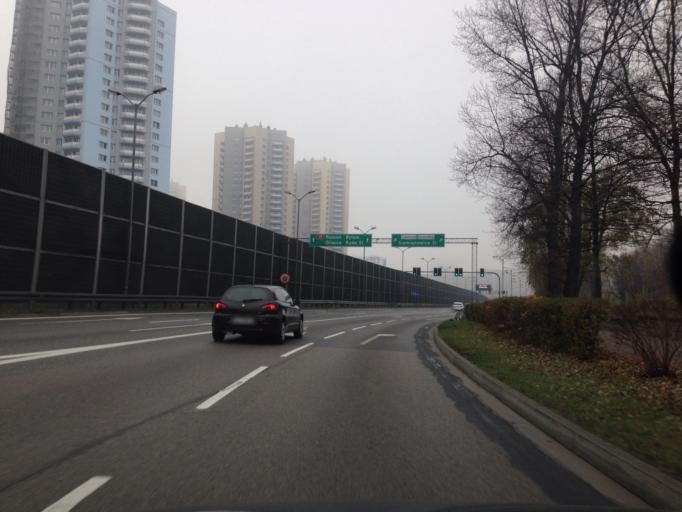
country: PL
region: Silesian Voivodeship
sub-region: Katowice
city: Katowice
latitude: 50.2621
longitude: 19.0422
